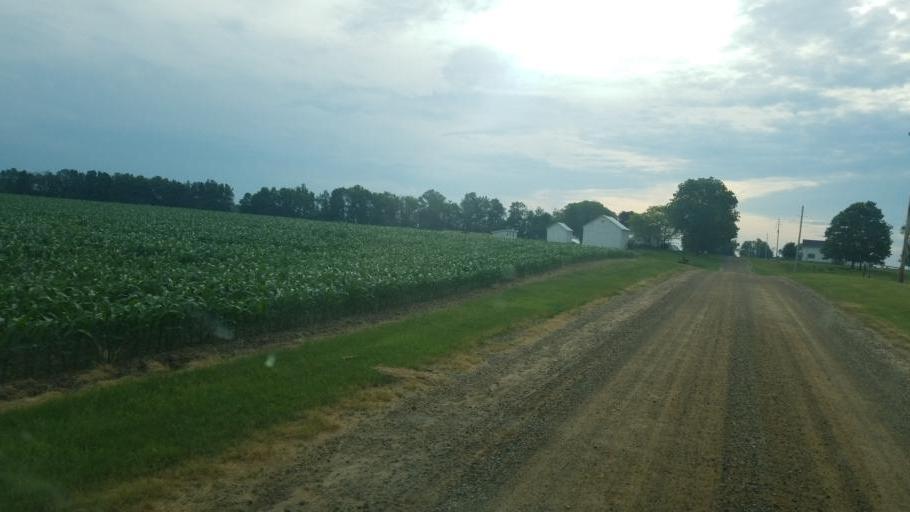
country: US
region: Michigan
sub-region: Eaton County
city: Charlotte
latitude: 42.6118
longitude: -84.9304
